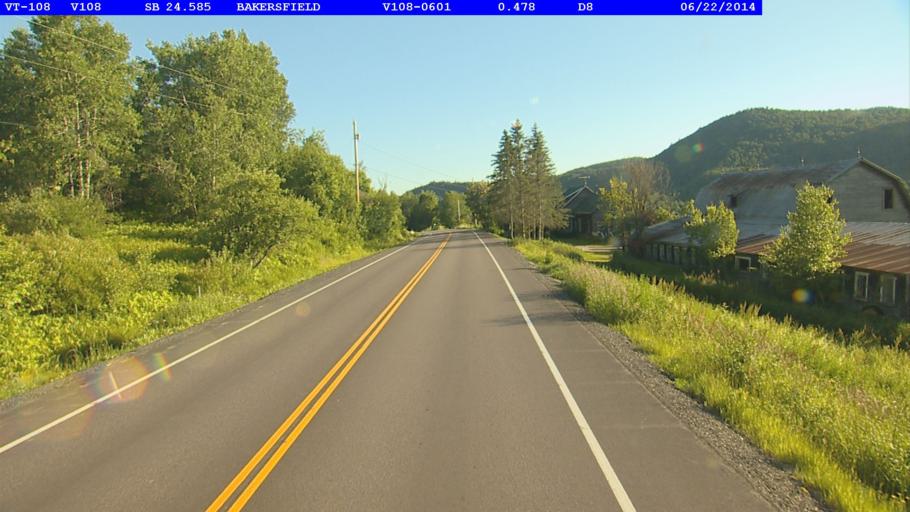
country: US
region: Vermont
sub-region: Franklin County
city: Enosburg Falls
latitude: 44.7402
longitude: -72.8244
